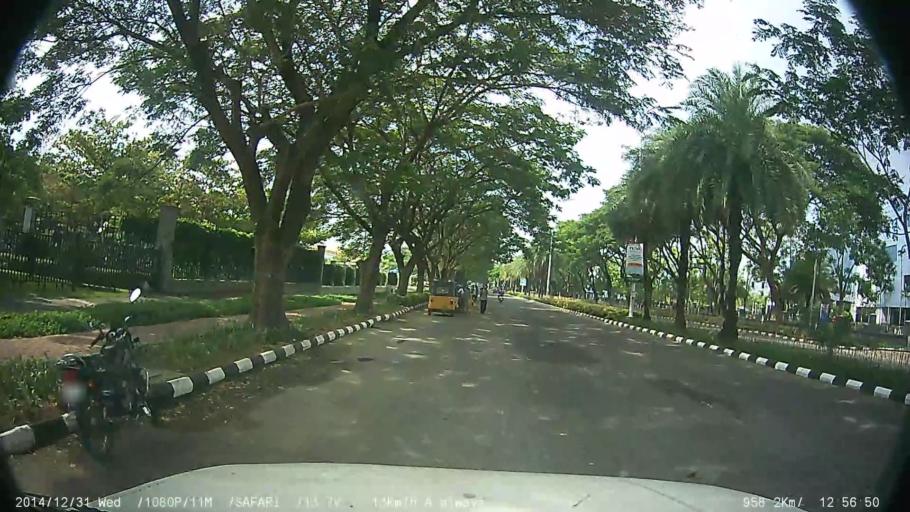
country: IN
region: Tamil Nadu
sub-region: Kancheepuram
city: Singapperumalkovil
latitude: 12.7360
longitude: 80.0077
